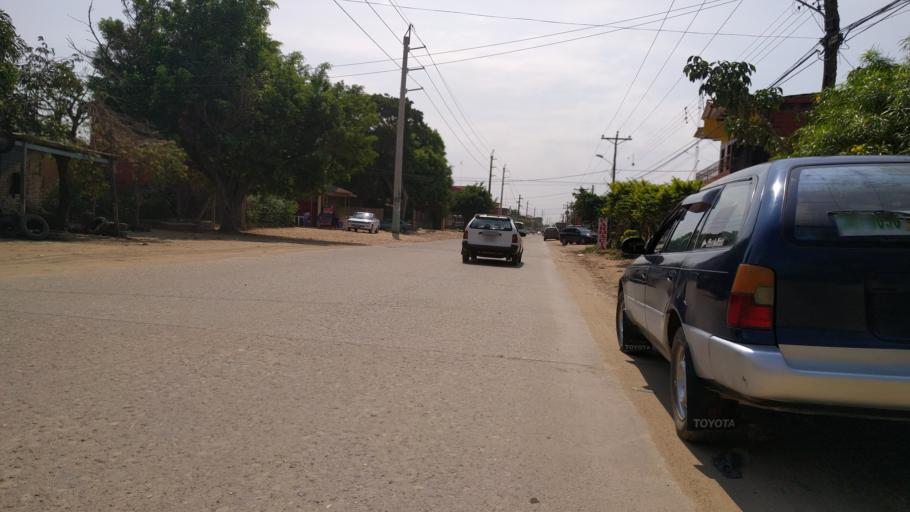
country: BO
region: Santa Cruz
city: Santa Cruz de la Sierra
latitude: -17.8507
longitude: -63.2187
